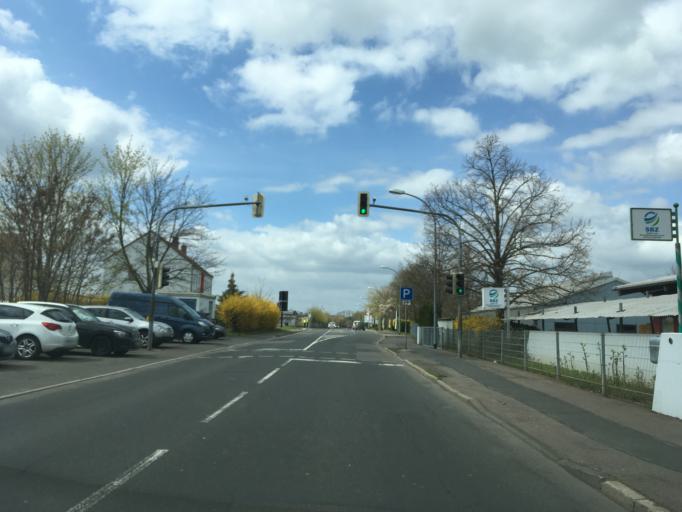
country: DE
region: Saxony
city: Delitzsch
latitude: 51.5179
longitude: 12.3299
